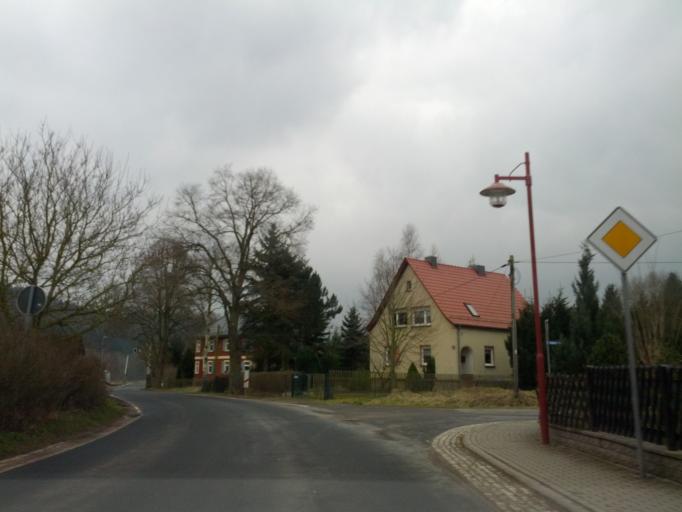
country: DE
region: Thuringia
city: Gerstungen
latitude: 50.9955
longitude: 10.0968
